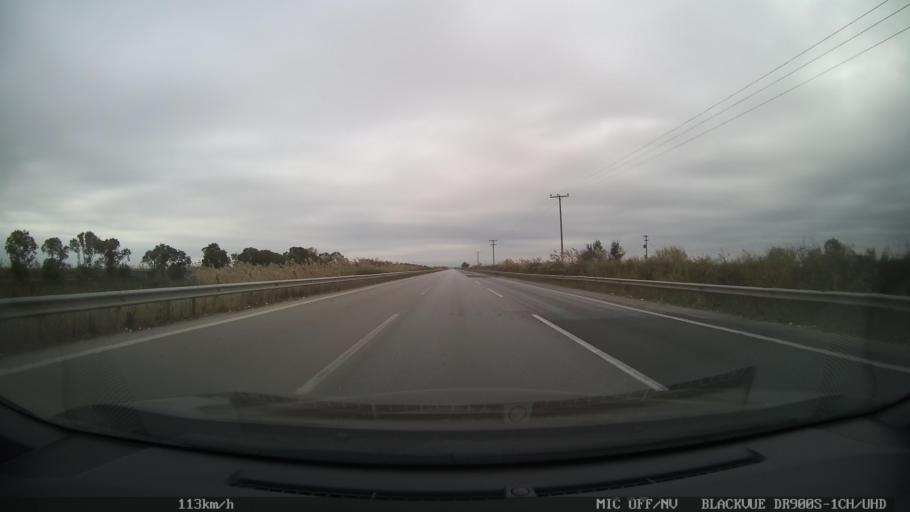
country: GR
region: Central Macedonia
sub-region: Nomos Thessalonikis
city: Nea Malgara
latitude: 40.5851
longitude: 22.6466
